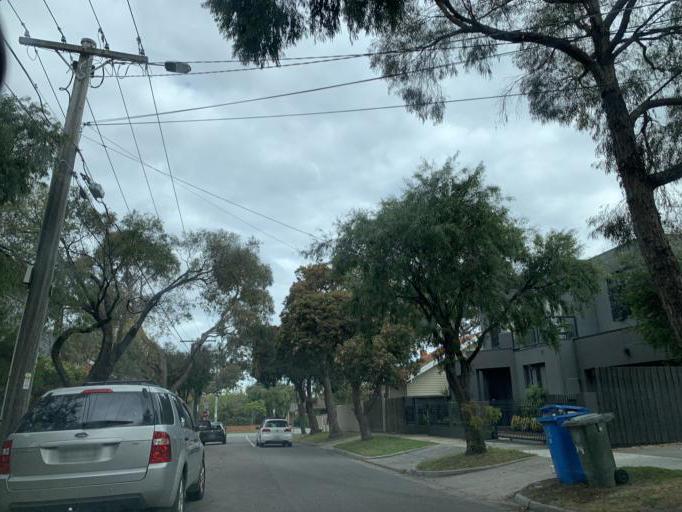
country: AU
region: Victoria
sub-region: Bayside
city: Black Rock
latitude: -37.9757
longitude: 145.0226
